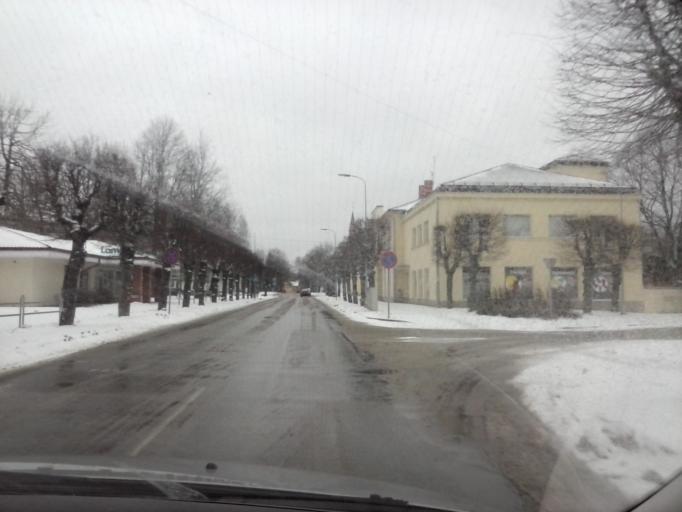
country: LV
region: Valkas Rajons
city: Valka
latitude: 57.7742
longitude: 26.0197
